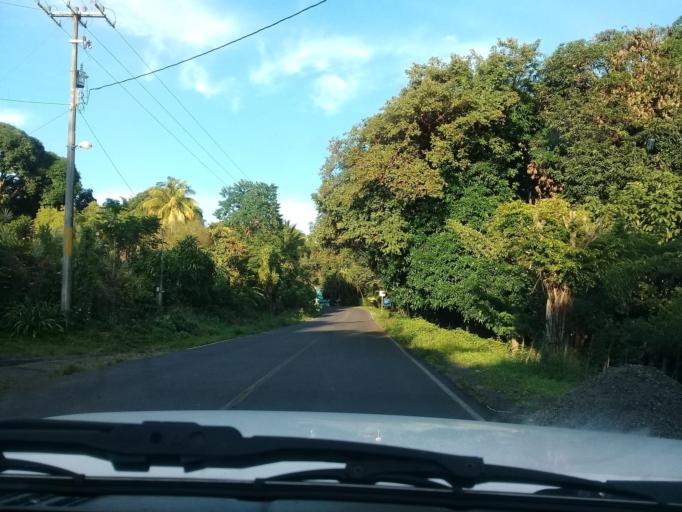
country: MX
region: Veracruz
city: Catemaco
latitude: 18.4298
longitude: -95.0926
